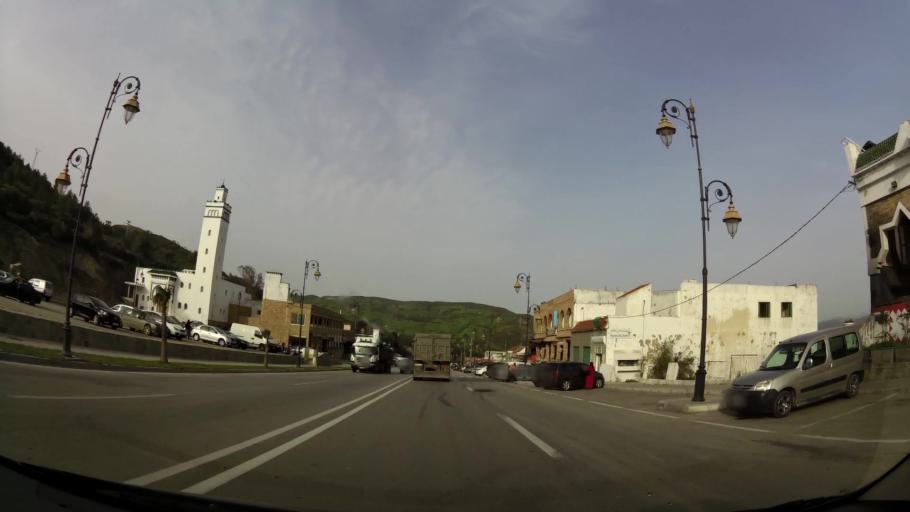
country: MA
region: Tanger-Tetouan
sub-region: Tetouan
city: Saddina
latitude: 35.5472
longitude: -5.5562
